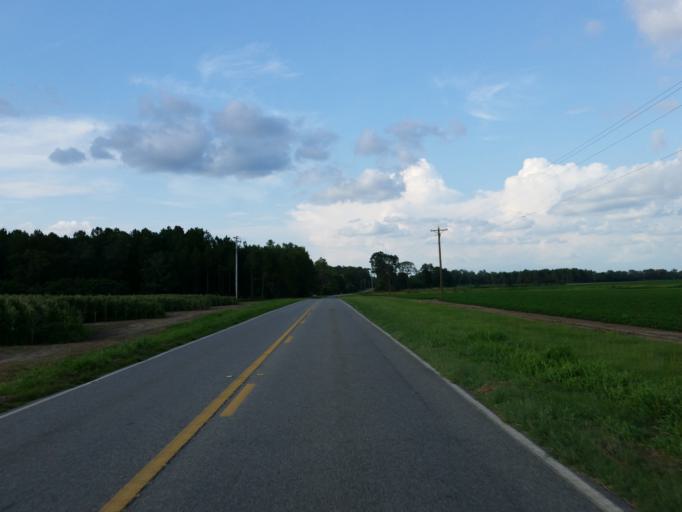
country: US
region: Georgia
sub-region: Crisp County
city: Cordele
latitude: 32.0147
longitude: -83.8496
